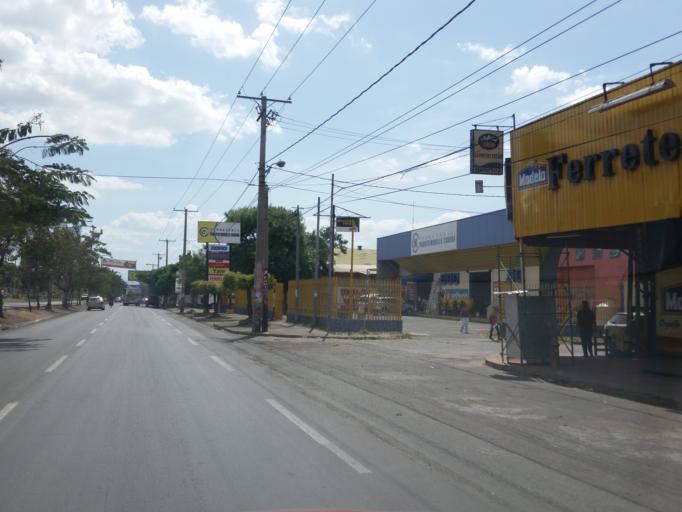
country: NI
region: Managua
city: Managua
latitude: 12.1526
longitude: -86.2451
